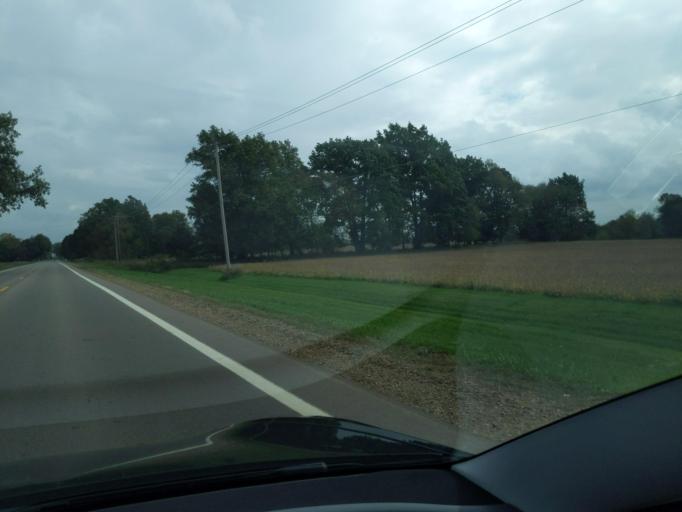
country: US
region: Michigan
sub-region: Eaton County
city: Eaton Rapids
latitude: 42.5207
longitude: -84.6834
